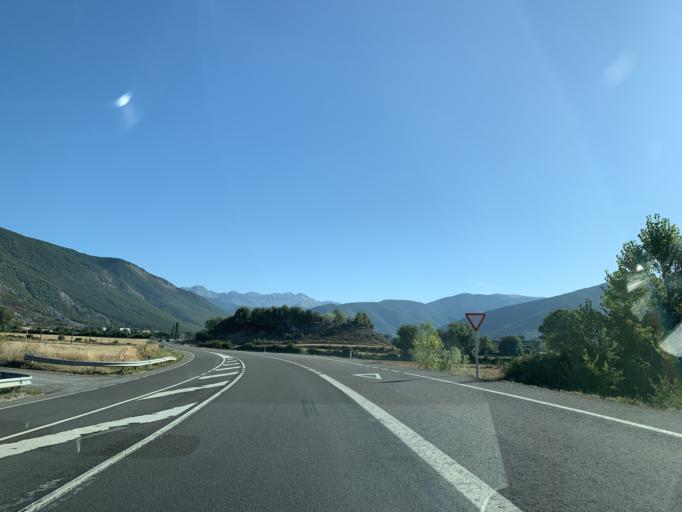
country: ES
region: Aragon
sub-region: Provincia de Huesca
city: Sabinanigo
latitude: 42.5416
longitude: -0.3535
